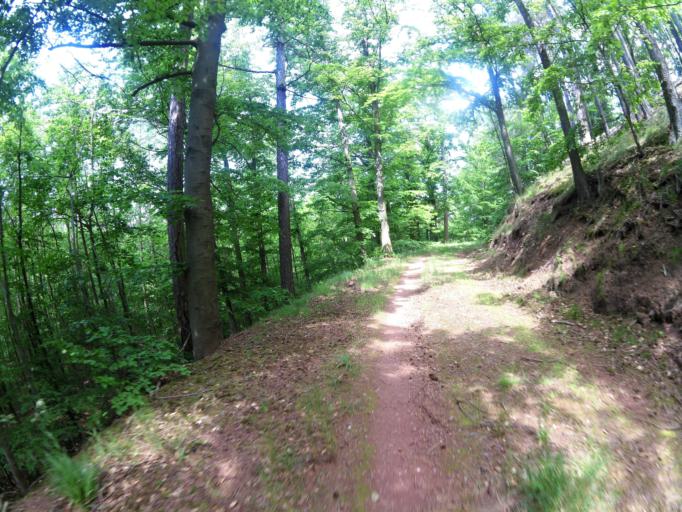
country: DE
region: Thuringia
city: Wolfsburg-Unkeroda
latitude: 50.9504
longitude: 10.2943
